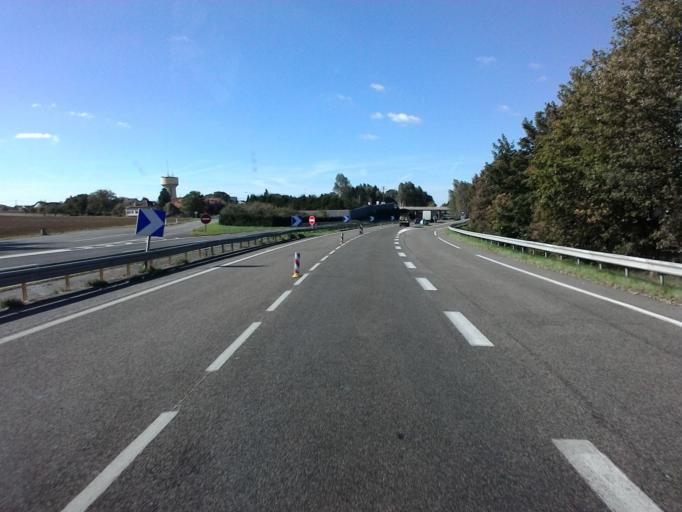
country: FR
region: Lorraine
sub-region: Departement de Meurthe-et-Moselle
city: Villers-la-Montagne
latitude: 49.4698
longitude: 5.8384
